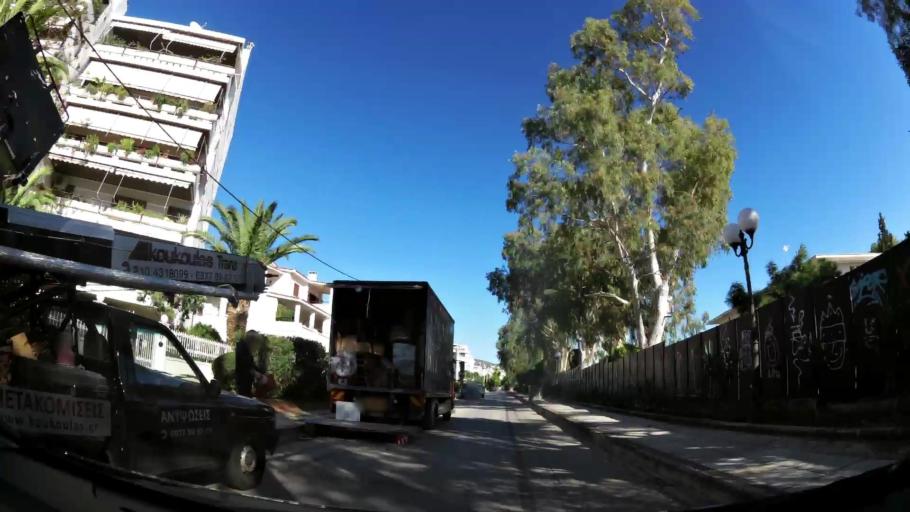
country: GR
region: Attica
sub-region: Nomarchia Athinas
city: Glyfada
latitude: 37.8495
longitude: 23.7572
